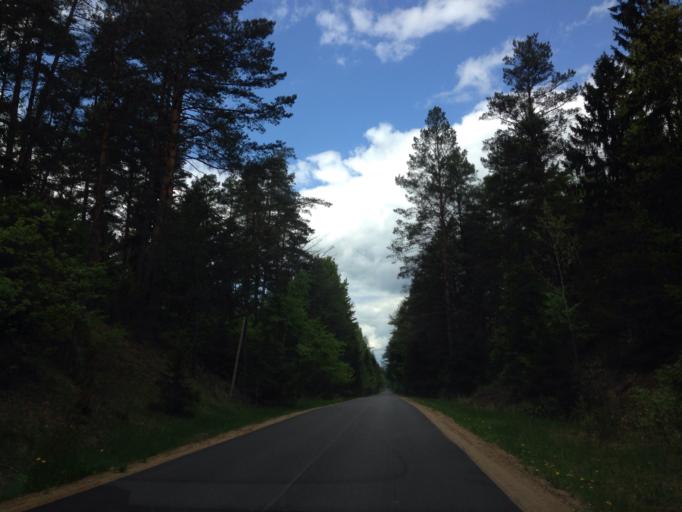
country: PL
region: Podlasie
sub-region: Powiat grajewski
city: Radzilow
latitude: 53.3336
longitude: 22.5994
